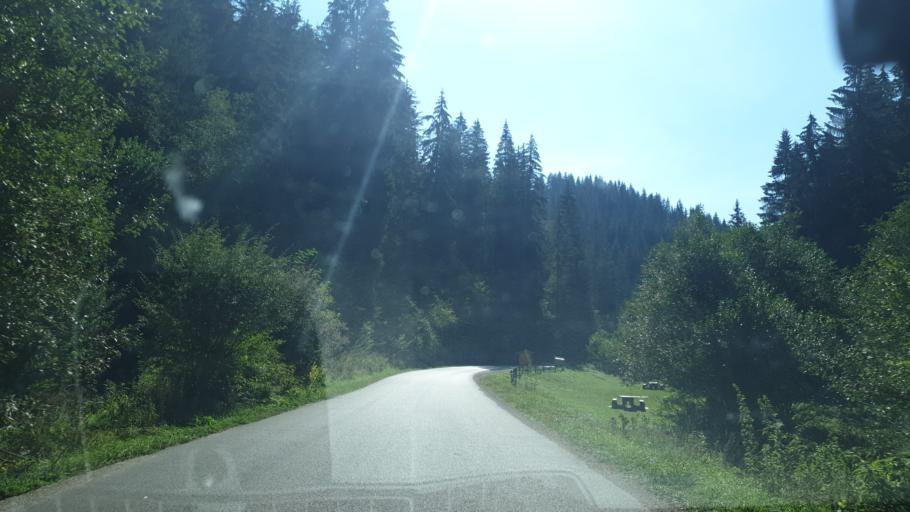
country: RS
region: Central Serbia
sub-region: Zlatiborski Okrug
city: Nova Varos
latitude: 43.4442
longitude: 19.8514
